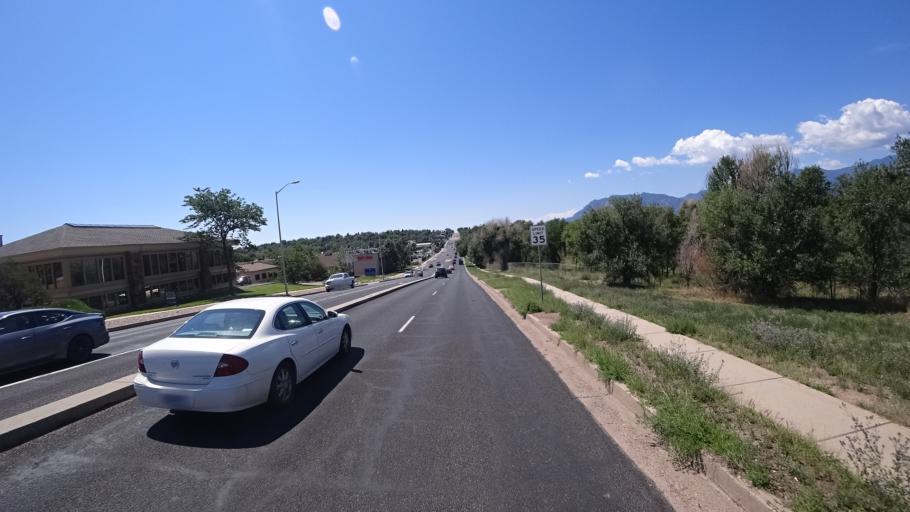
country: US
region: Colorado
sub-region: El Paso County
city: Colorado Springs
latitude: 38.8611
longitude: -104.7943
